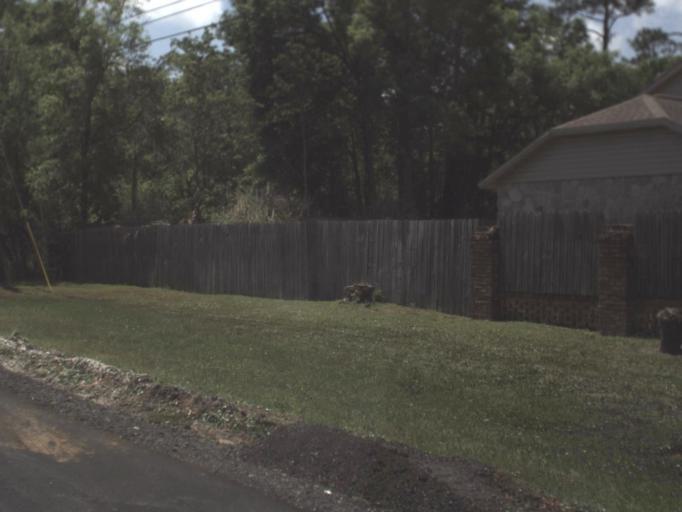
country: US
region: Florida
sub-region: Escambia County
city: Myrtle Grove
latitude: 30.4088
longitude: -87.3177
